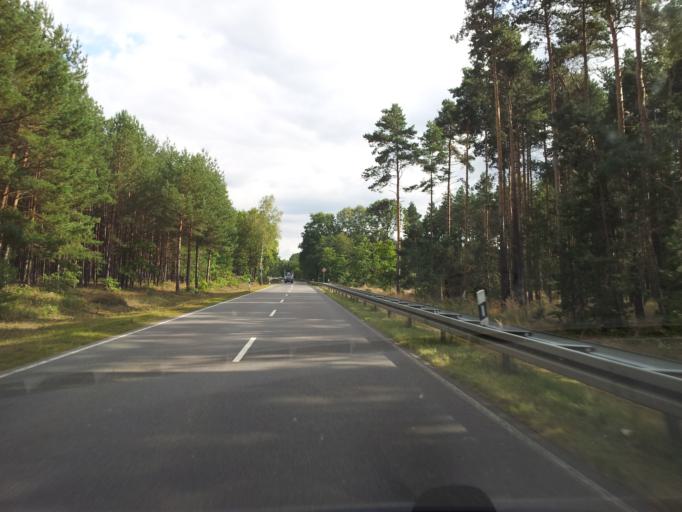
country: DE
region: Brandenburg
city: Ruhland
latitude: 51.4420
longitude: 13.8965
